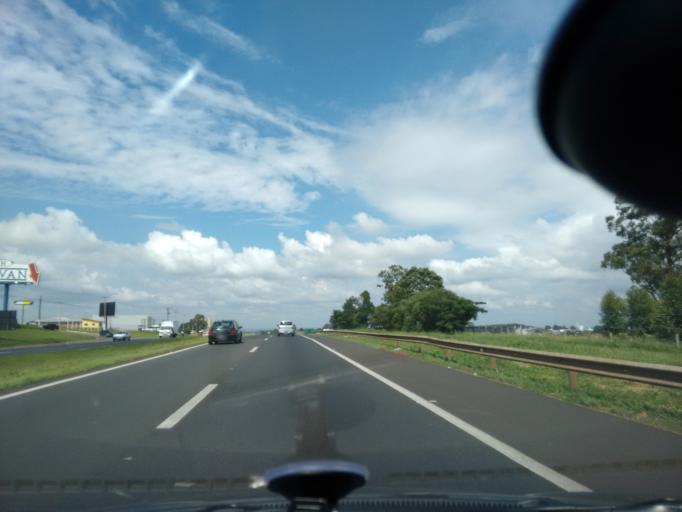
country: BR
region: Sao Paulo
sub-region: Sao Carlos
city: Sao Carlos
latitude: -22.0229
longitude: -47.8585
